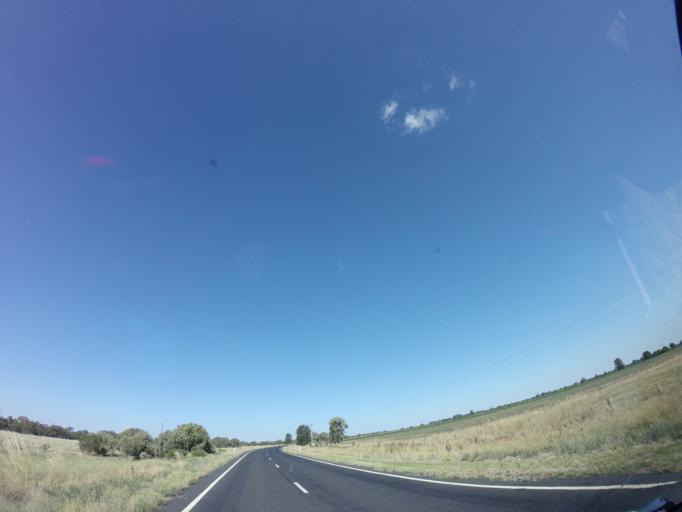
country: AU
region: New South Wales
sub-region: Gilgandra
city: Gilgandra
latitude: -31.6645
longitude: 148.1746
